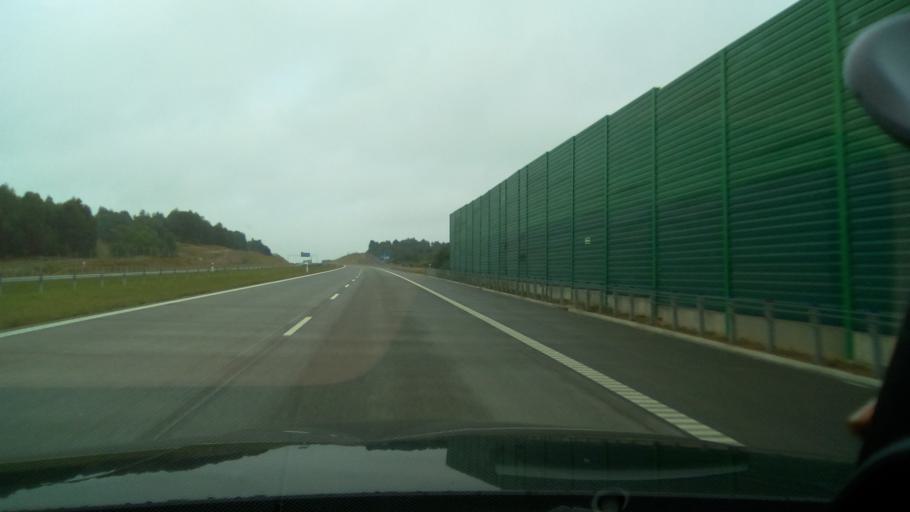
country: PL
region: Silesian Voivodeship
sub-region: Powiat klobucki
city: Kalej
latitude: 50.8365
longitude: 19.0308
